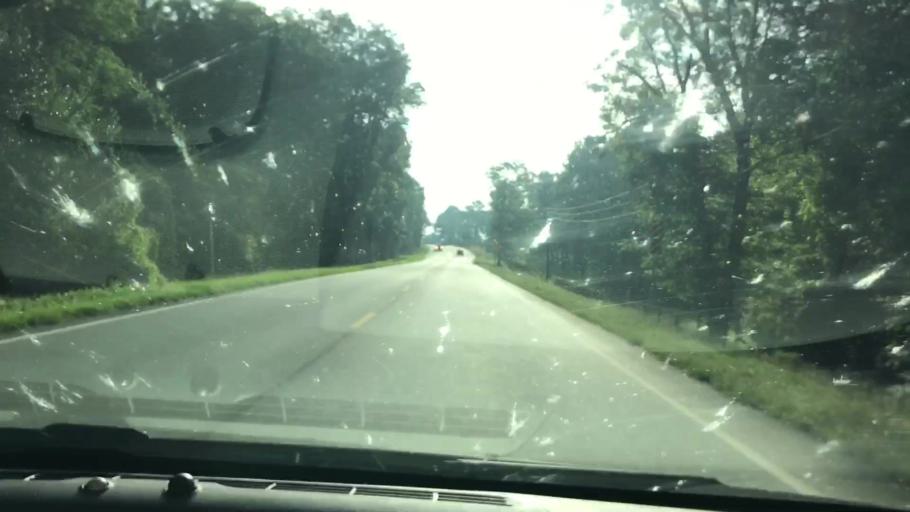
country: US
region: Georgia
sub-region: Terrell County
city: Dawson
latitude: 31.7693
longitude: -84.4658
